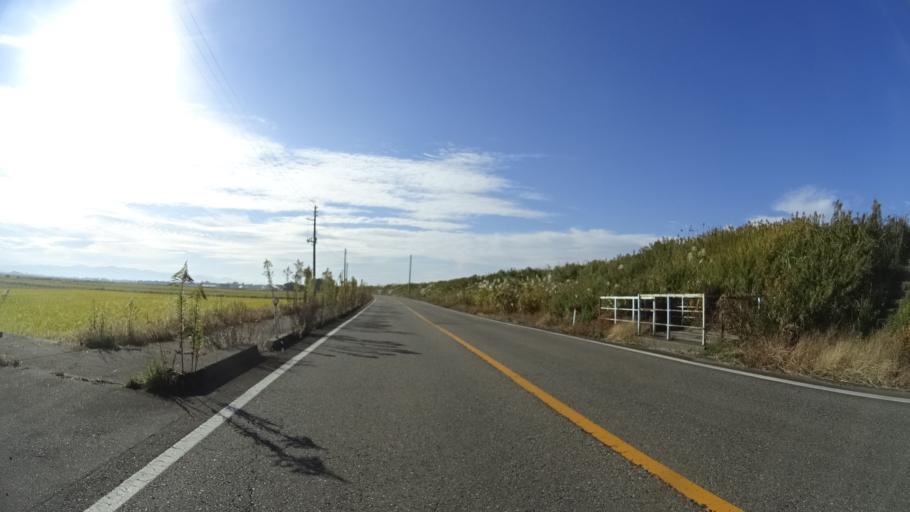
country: JP
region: Niigata
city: Yoshida-kasugacho
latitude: 37.5871
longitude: 138.8355
